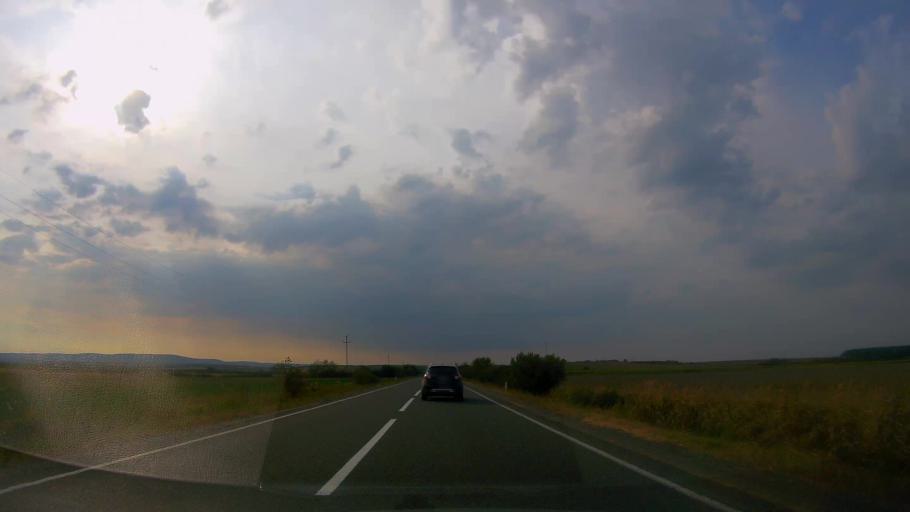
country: RO
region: Satu Mare
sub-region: Oras Ardud
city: Ardud
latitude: 47.6211
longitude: 22.8717
